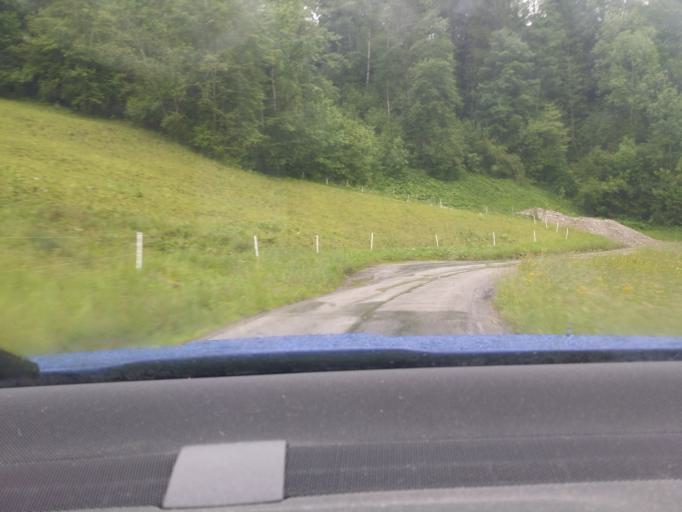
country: AT
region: Salzburg
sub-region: Politischer Bezirk Hallein
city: Abtenau
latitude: 47.5777
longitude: 13.3701
